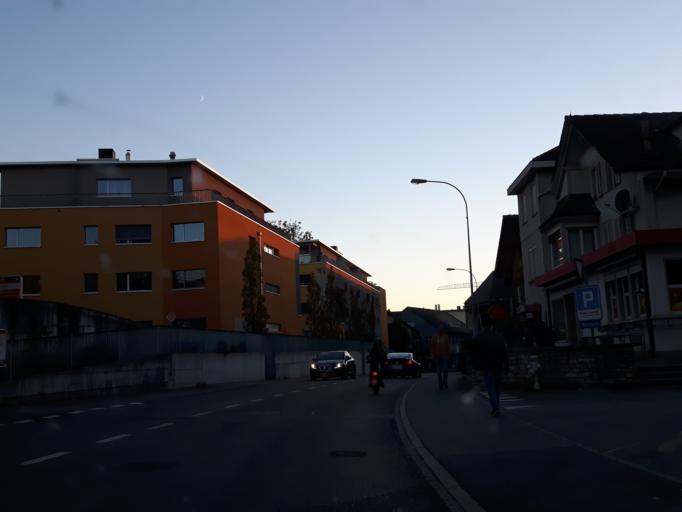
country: CH
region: Bern
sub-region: Oberaargau
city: Langenthal
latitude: 47.2137
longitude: 7.7935
